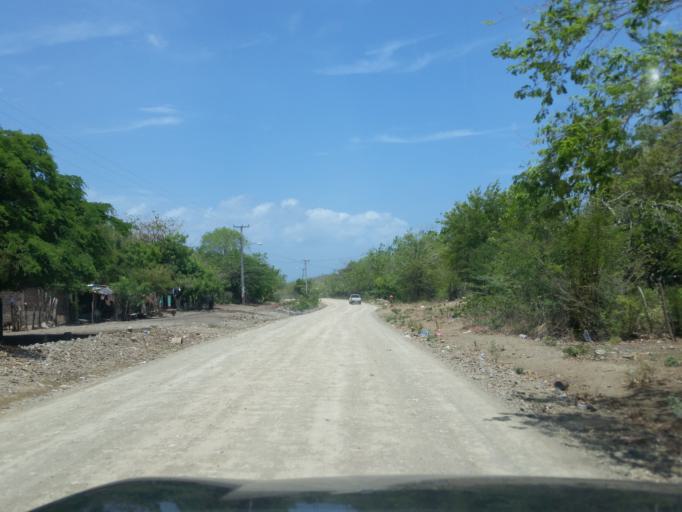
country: NI
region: Rivas
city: Tola
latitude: 11.4742
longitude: -86.1047
